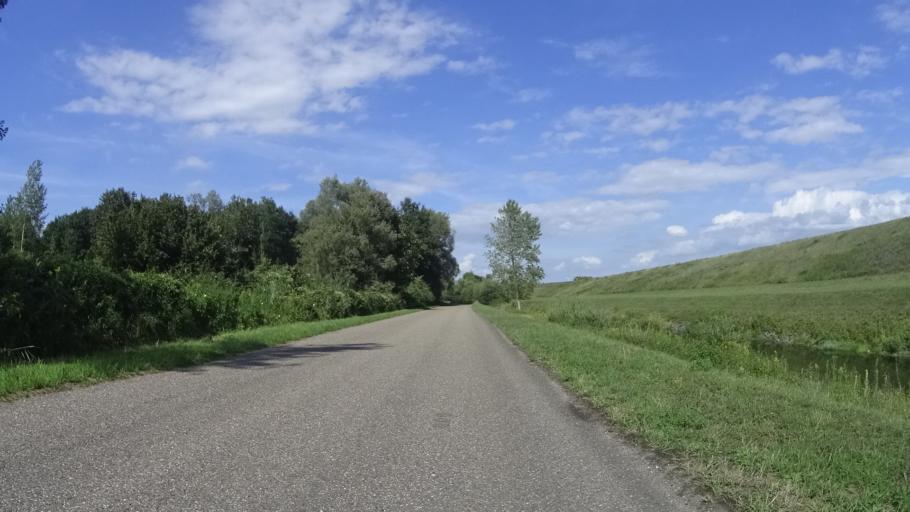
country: DE
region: Baden-Wuerttemberg
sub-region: Karlsruhe Region
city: Hugelsheim
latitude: 48.7978
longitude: 8.0774
